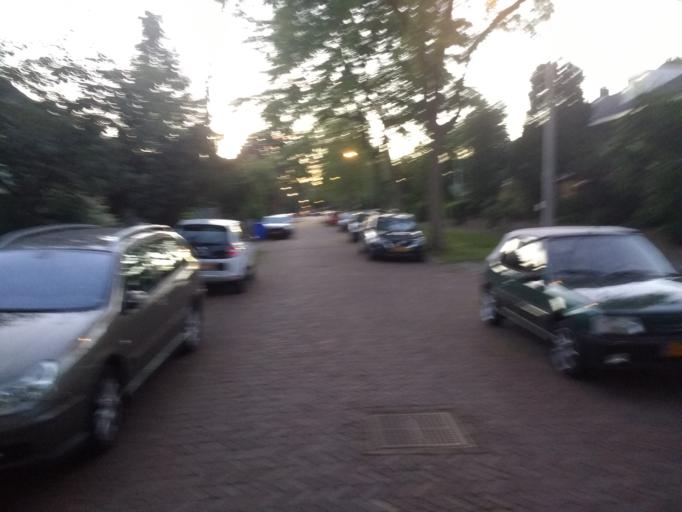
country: NL
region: South Holland
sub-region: Gemeente Voorschoten
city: Voorschoten
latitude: 52.1320
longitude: 4.4541
